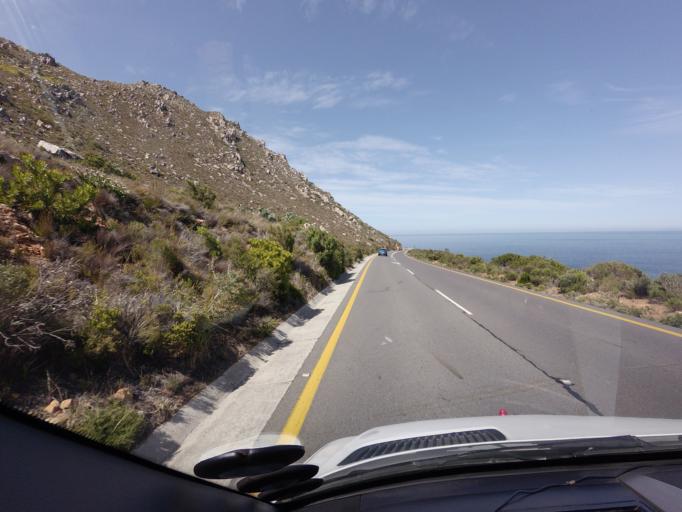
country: ZA
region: Western Cape
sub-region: Overberg District Municipality
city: Grabouw
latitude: -34.2117
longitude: 18.8351
